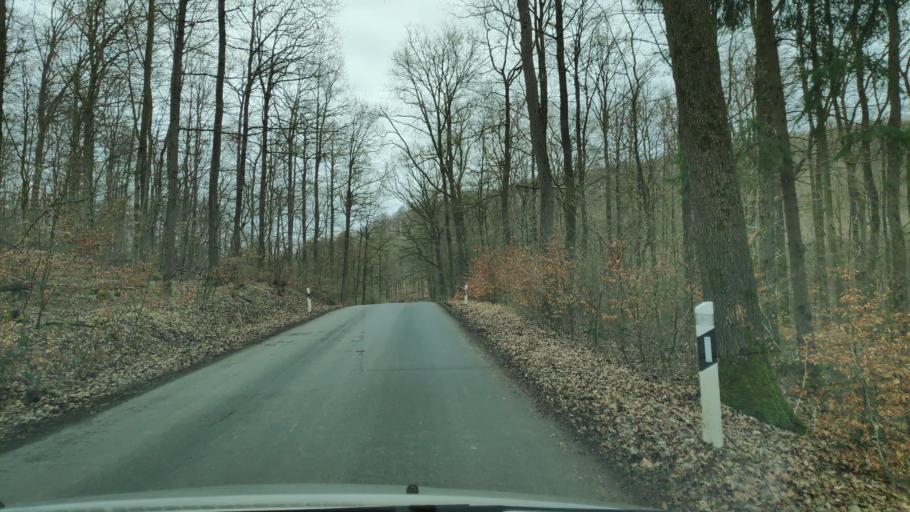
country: DE
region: Lower Saxony
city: Hessisch Oldendorf
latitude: 52.1970
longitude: 9.2839
